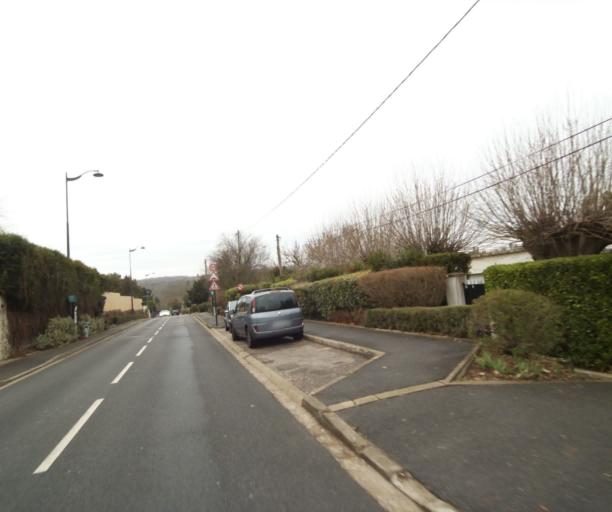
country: FR
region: Ile-de-France
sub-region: Departement des Yvelines
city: Bougival
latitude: 48.8645
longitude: 2.1663
